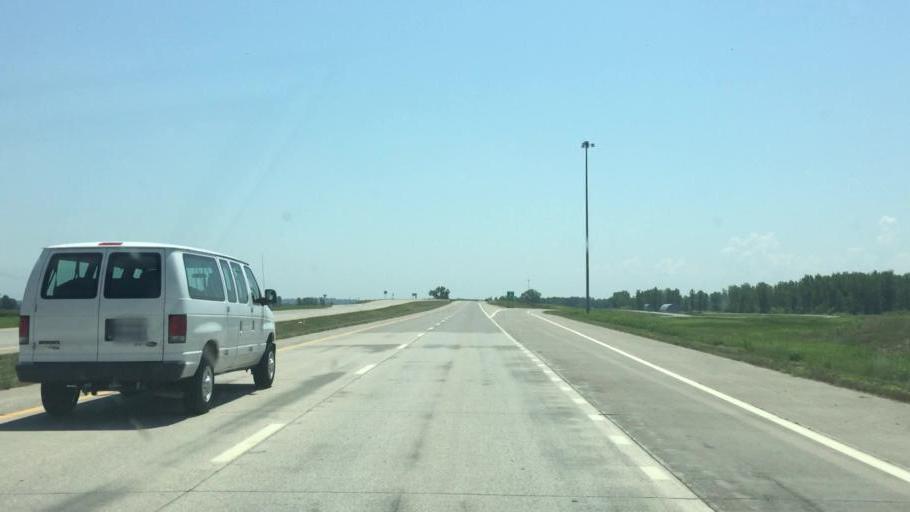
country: US
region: Kansas
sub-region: Doniphan County
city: Wathena
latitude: 39.7503
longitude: -94.9296
